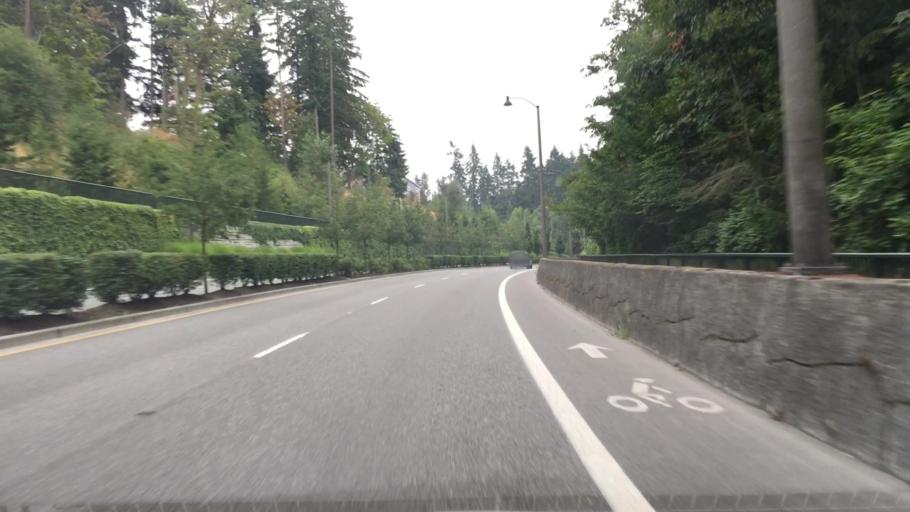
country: US
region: Washington
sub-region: King County
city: Newcastle
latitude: 47.5226
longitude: -122.1603
